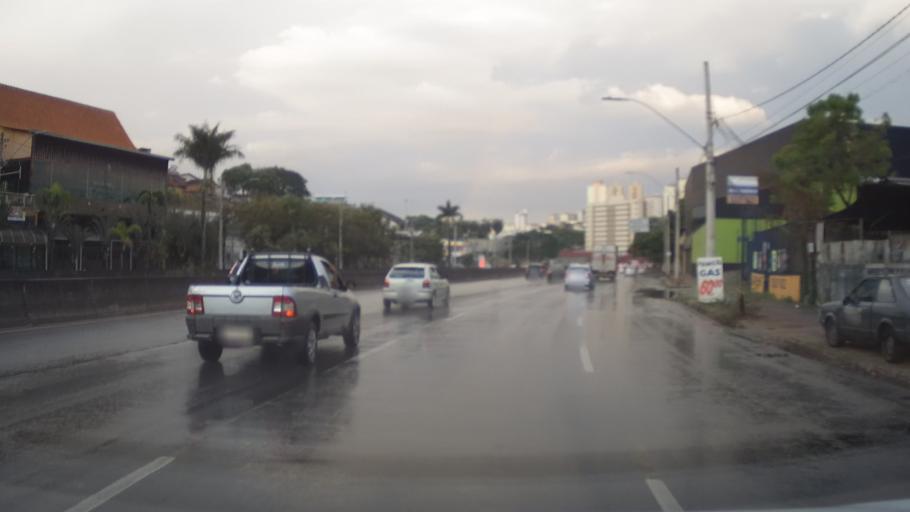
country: BR
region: Minas Gerais
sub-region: Belo Horizonte
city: Belo Horizonte
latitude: -19.9422
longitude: -43.9874
